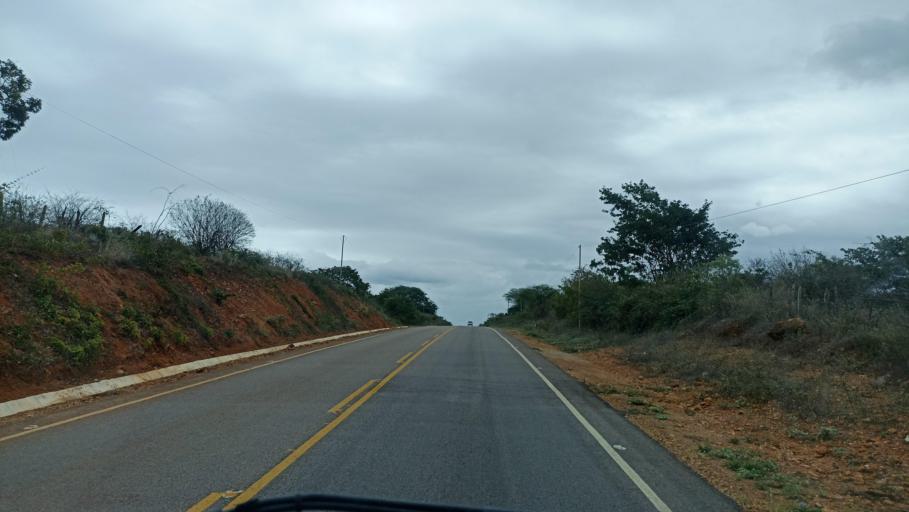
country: BR
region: Bahia
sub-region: Andarai
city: Vera Cruz
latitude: -12.9918
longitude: -41.0010
